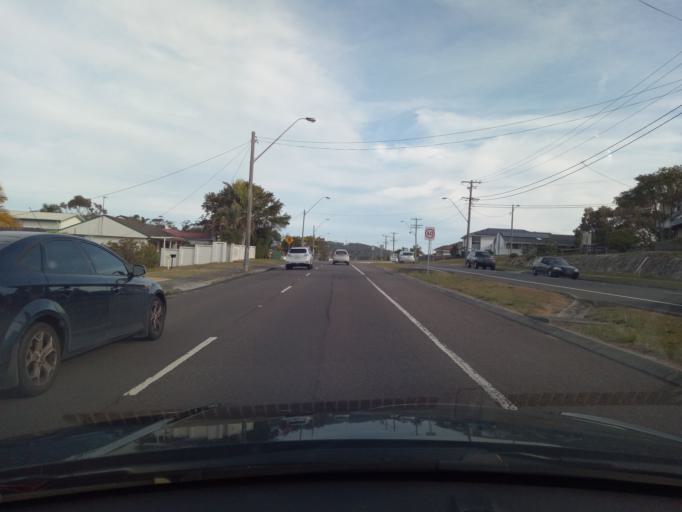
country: AU
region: New South Wales
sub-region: Wyong Shire
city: Bateau Bay
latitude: -33.3874
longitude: 151.4730
